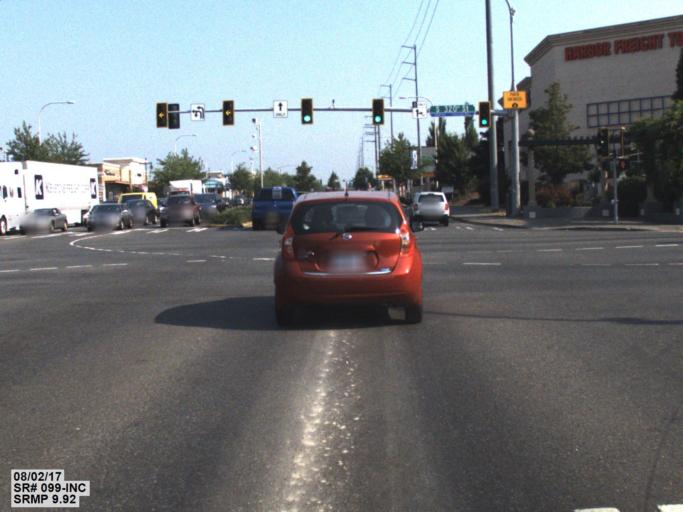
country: US
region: Washington
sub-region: King County
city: Federal Way
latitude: 47.3149
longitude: -122.3133
